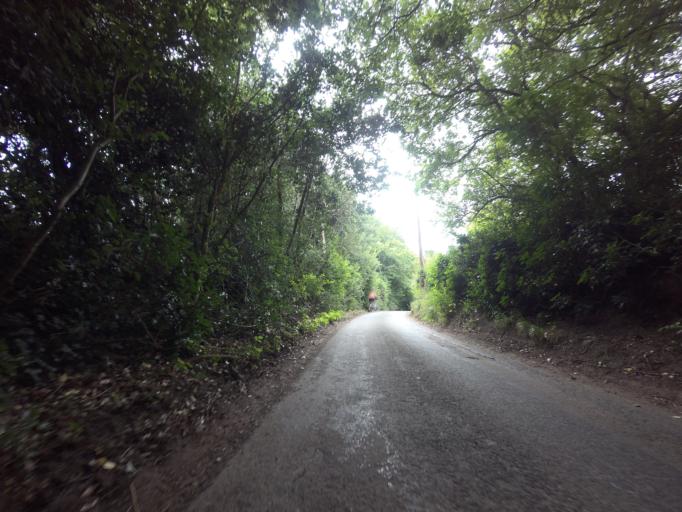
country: GB
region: England
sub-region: Kent
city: Swanley
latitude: 51.3648
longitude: 0.1510
